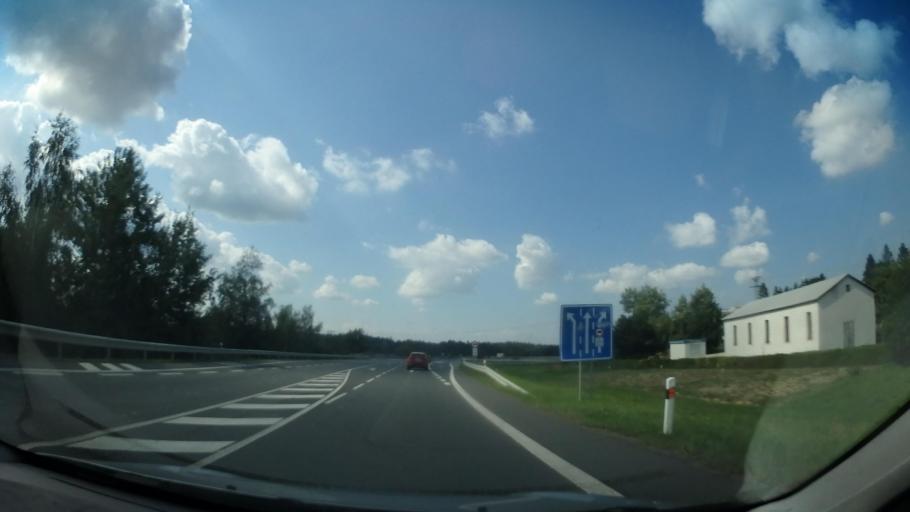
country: CZ
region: Central Bohemia
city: Kostelec nad Cernymi Lesy
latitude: 49.9850
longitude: 14.8493
